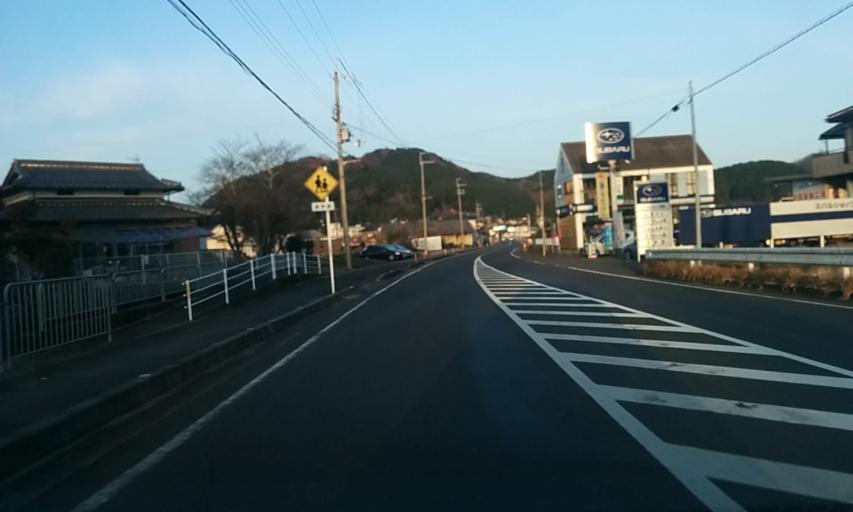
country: JP
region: Kyoto
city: Ayabe
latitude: 35.3124
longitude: 135.2209
